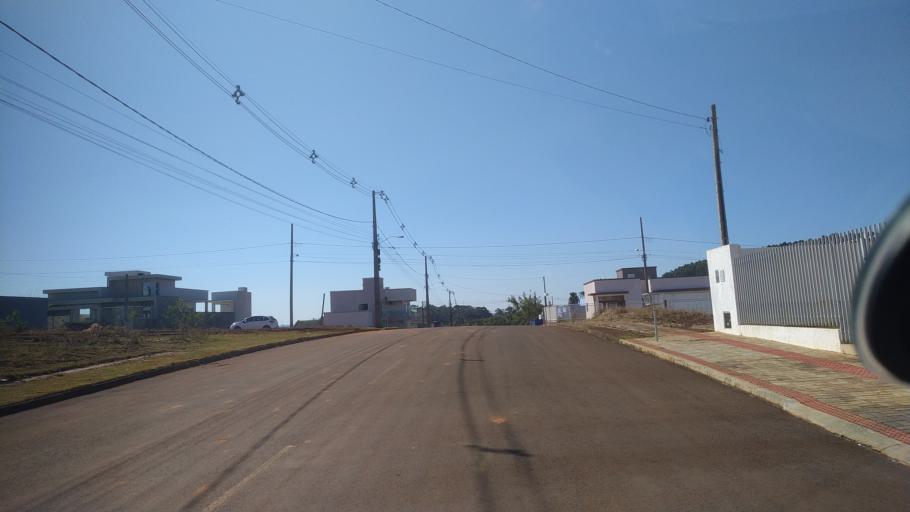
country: BR
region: Santa Catarina
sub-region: Chapeco
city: Chapeco
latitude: -27.0900
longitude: -52.5810
